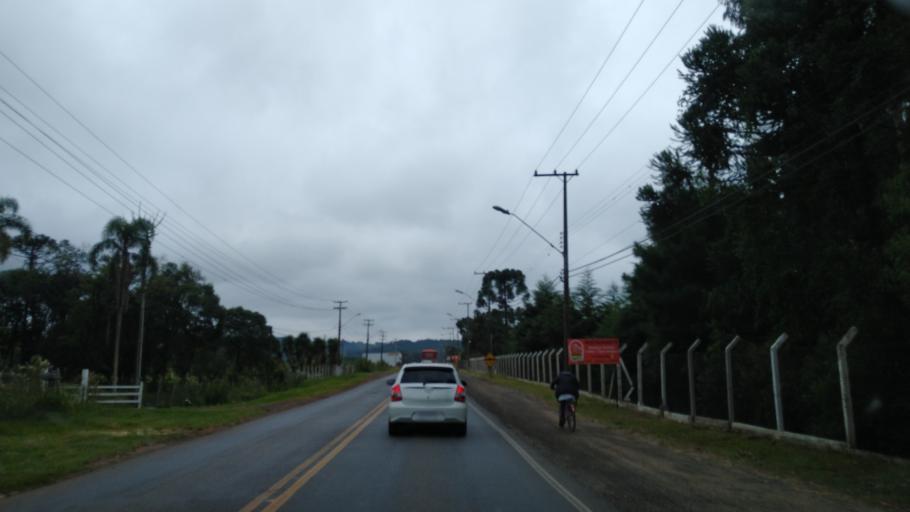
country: BR
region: Parana
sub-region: Uniao Da Vitoria
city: Uniao da Vitoria
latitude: -26.2470
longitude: -51.1213
